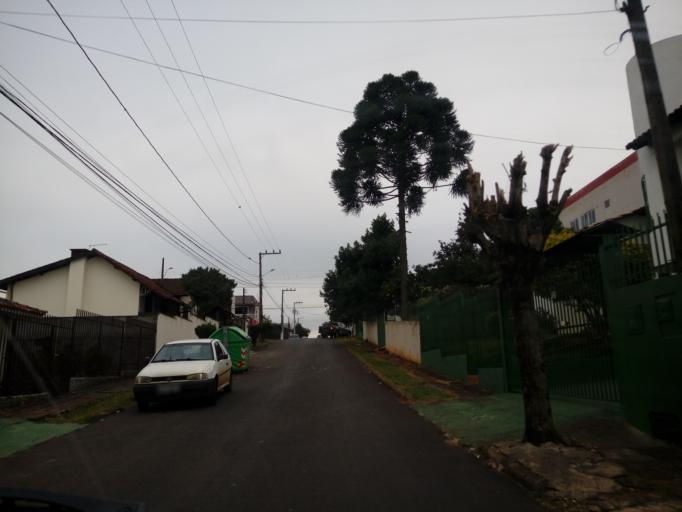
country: BR
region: Santa Catarina
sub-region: Chapeco
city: Chapeco
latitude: -27.0921
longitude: -52.6297
